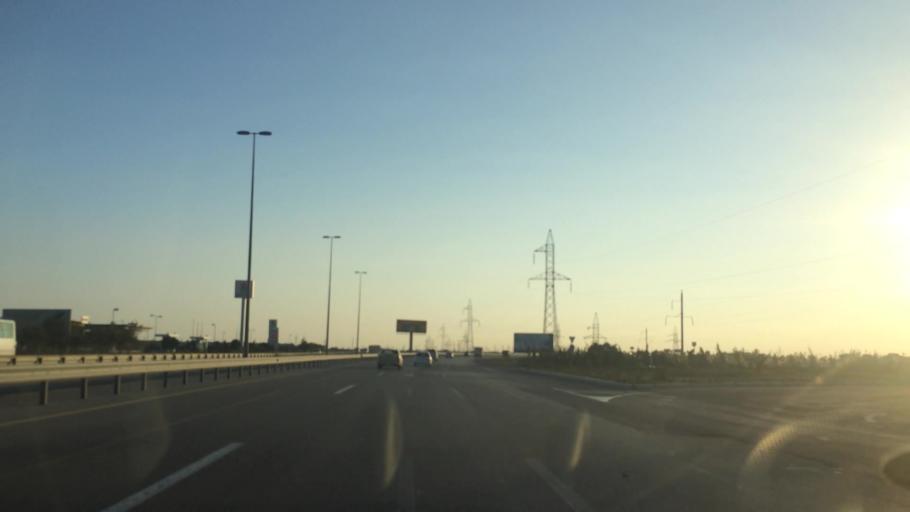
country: AZ
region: Baki
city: Qobustan
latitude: 39.9721
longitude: 49.4159
